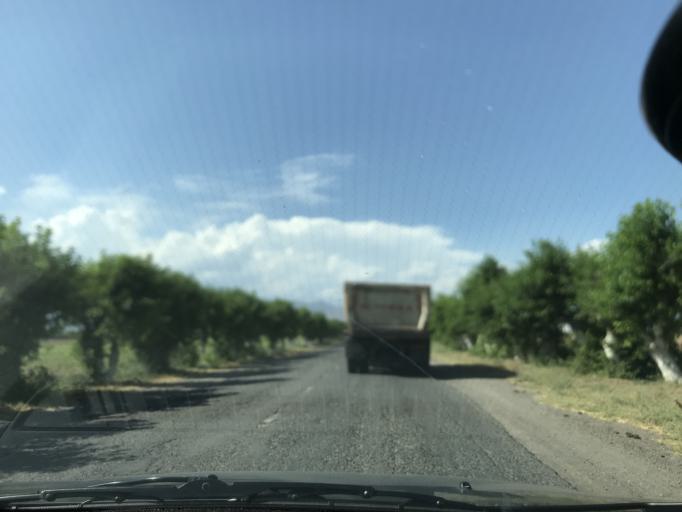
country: UZ
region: Namangan
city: Chust Shahri
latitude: 41.0525
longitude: 71.2096
